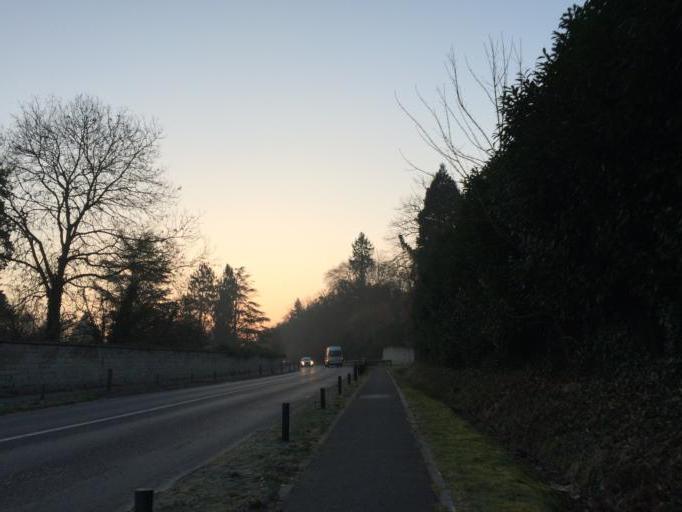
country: FR
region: Picardie
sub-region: Departement de l'Oise
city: Lamorlaye
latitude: 49.1437
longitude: 2.4493
